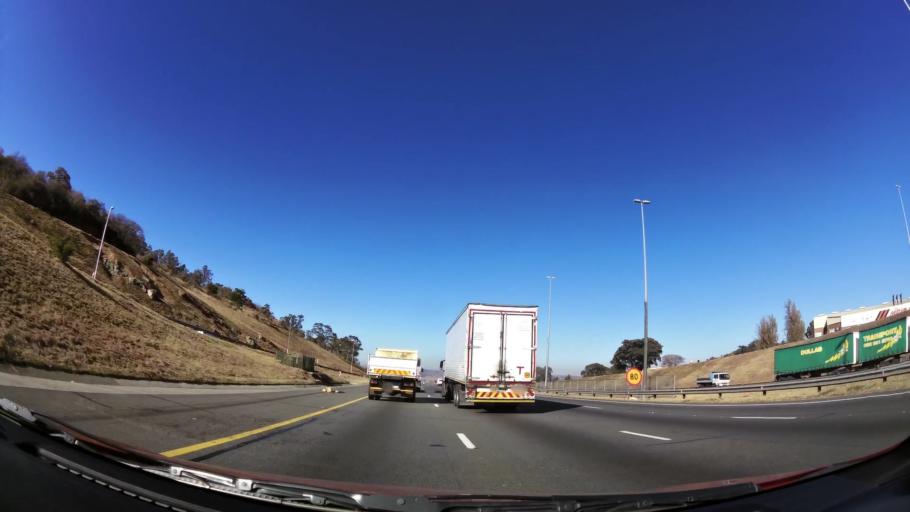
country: ZA
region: Gauteng
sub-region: City of Johannesburg Metropolitan Municipality
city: Soweto
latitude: -26.2783
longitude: 27.9473
